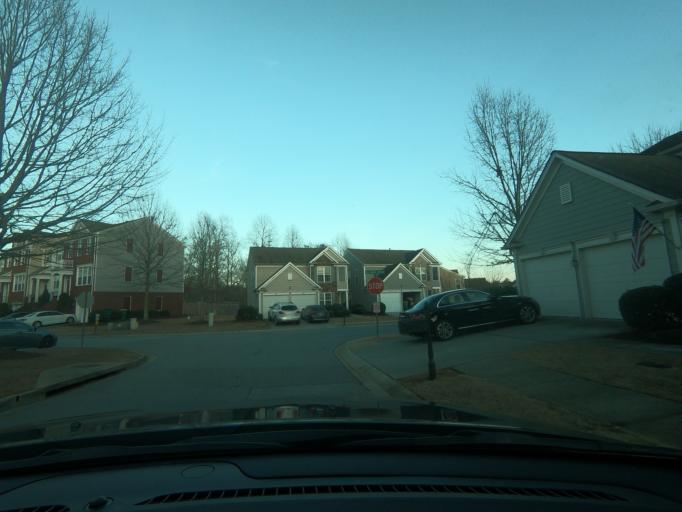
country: US
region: Georgia
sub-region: Cherokee County
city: Woodstock
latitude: 34.0864
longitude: -84.4602
